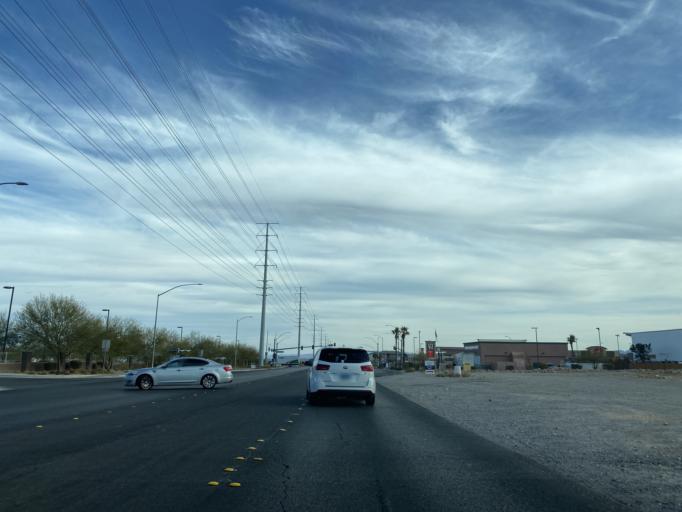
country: US
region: Nevada
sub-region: Clark County
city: Enterprise
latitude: 36.0556
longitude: -115.2633
